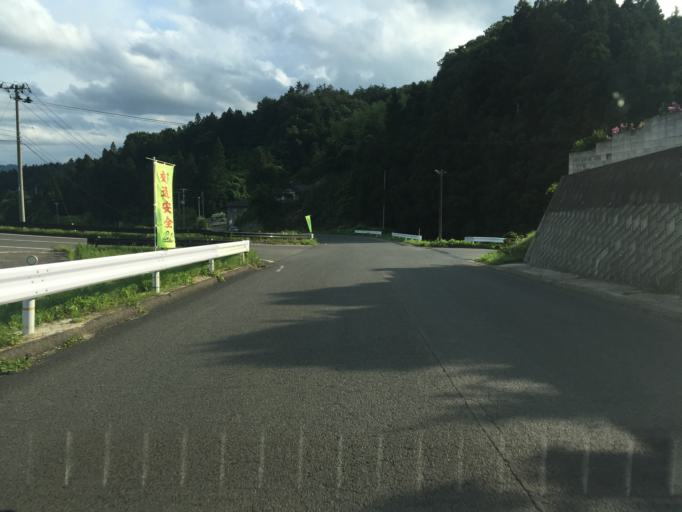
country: JP
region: Fukushima
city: Fukushima-shi
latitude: 37.6965
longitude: 140.5727
